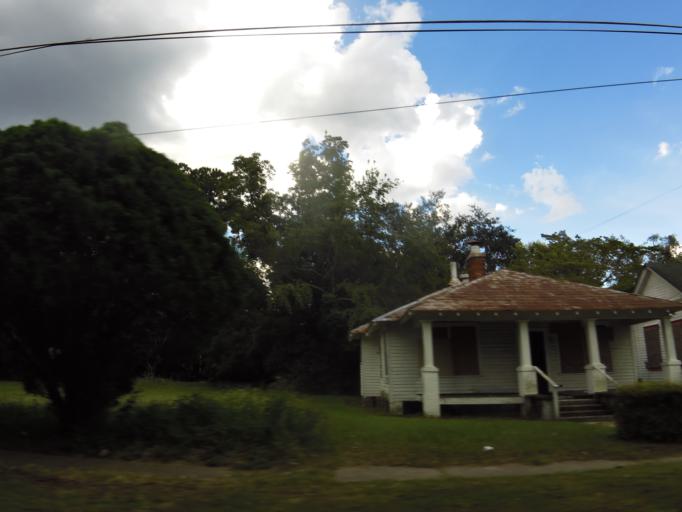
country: US
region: Georgia
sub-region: Lowndes County
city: Valdosta
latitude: 30.8376
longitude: -83.2780
